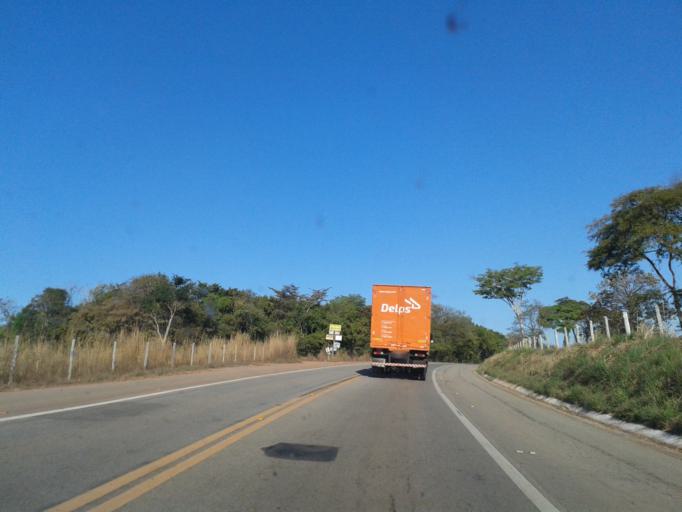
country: BR
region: Goias
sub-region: Itapirapua
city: Itapirapua
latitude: -15.3042
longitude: -50.4454
